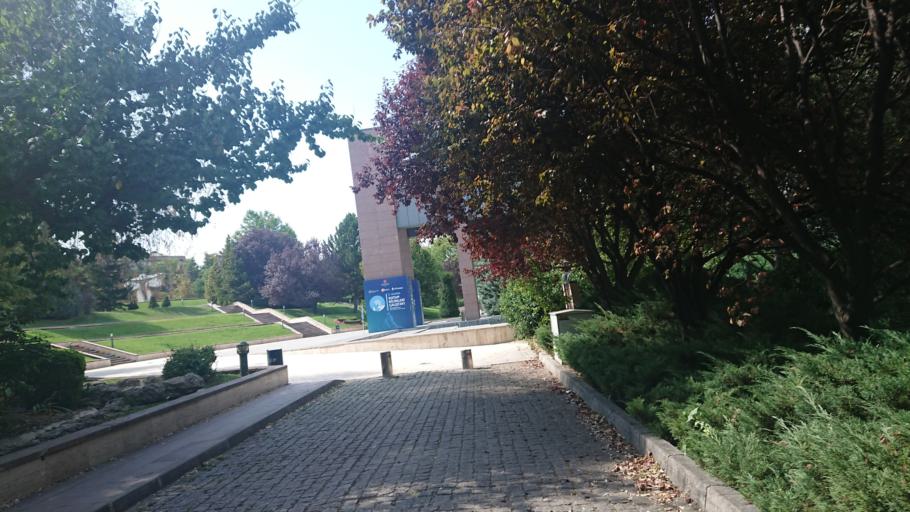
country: TR
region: Ankara
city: Ankara
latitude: 39.8936
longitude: 32.7863
